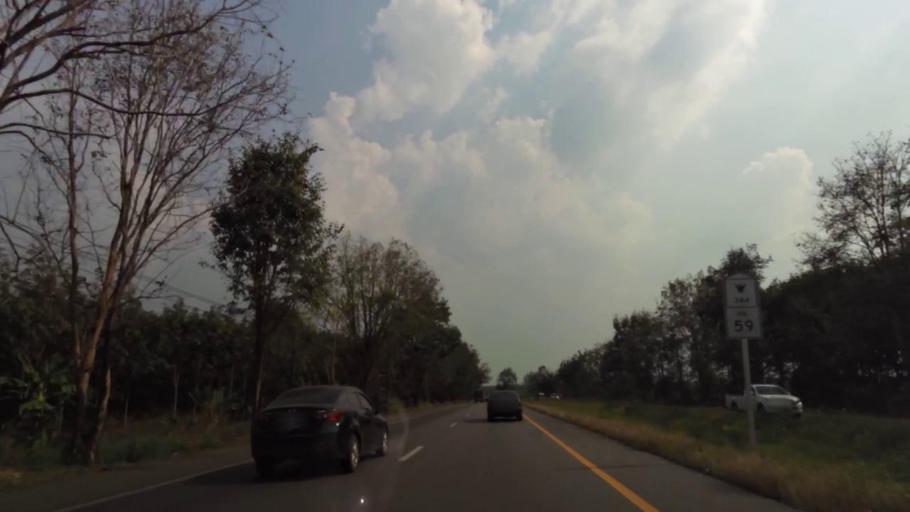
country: TH
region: Chon Buri
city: Nong Yai
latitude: 13.0716
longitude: 101.4122
